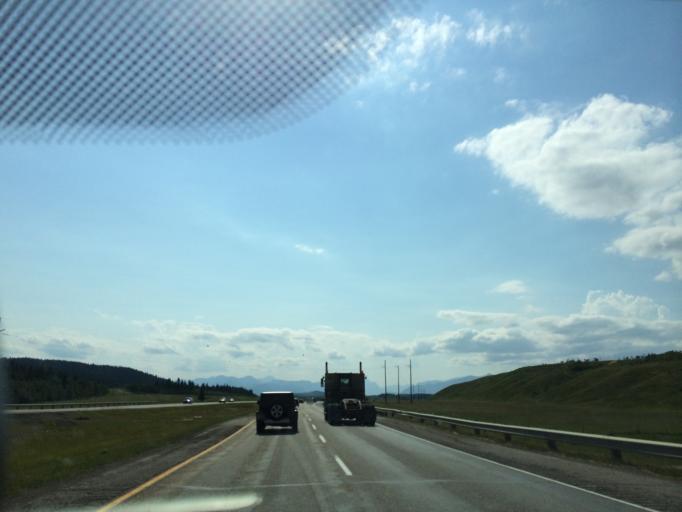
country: CA
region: Alberta
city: Cochrane
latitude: 51.1523
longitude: -114.8097
